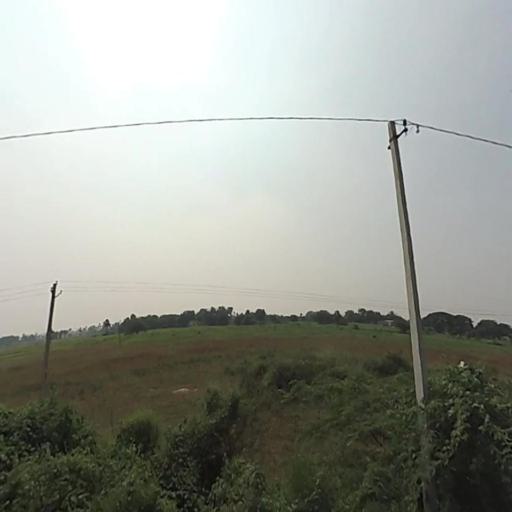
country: IN
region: Telangana
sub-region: Nalgonda
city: Nalgonda
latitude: 17.1835
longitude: 79.1248
